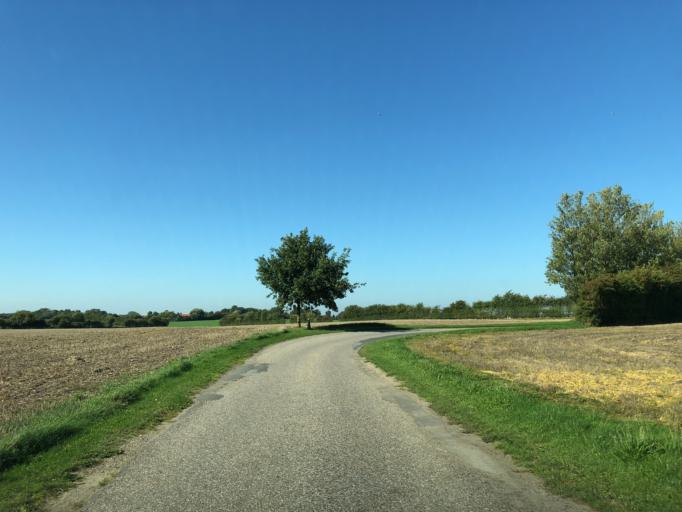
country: DK
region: South Denmark
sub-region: Sonderborg Kommune
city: Dybbol
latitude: 54.9465
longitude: 9.7304
